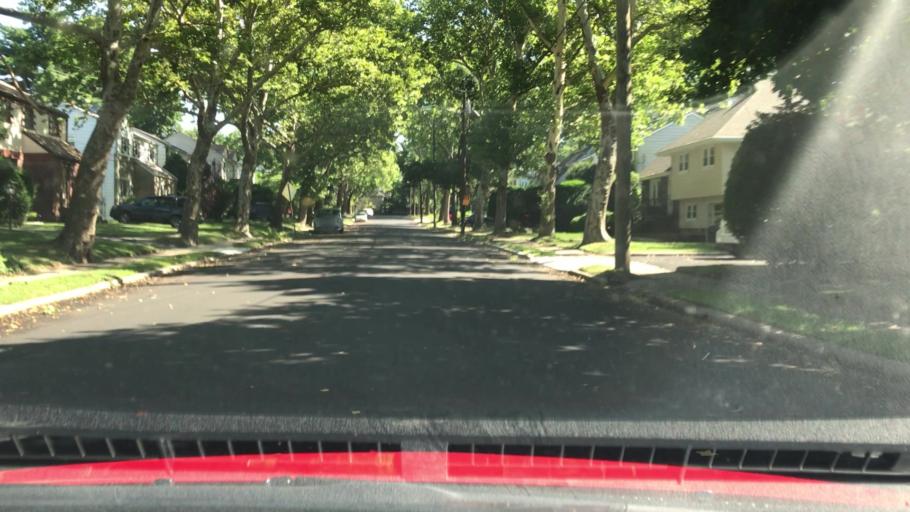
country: US
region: New Jersey
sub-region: Bergen County
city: Teaneck
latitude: 40.8803
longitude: -74.0015
